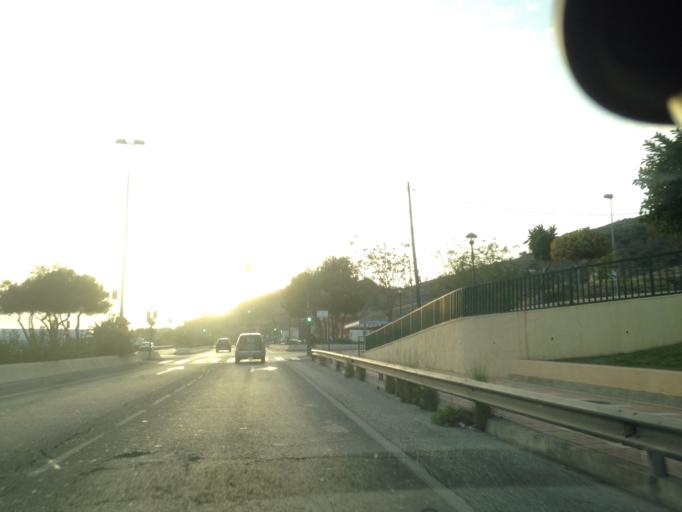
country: ES
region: Andalusia
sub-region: Provincia de Malaga
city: Malaga
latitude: 36.7366
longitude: -4.4323
